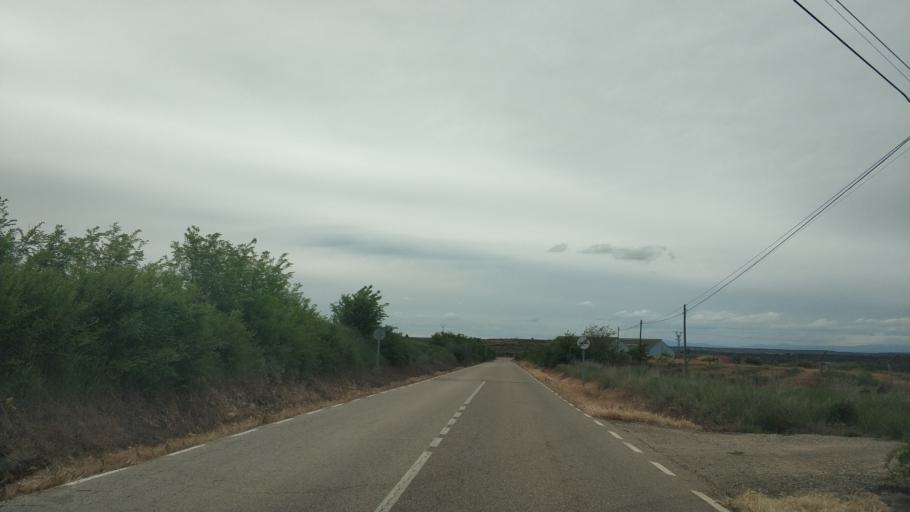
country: ES
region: Castille and Leon
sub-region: Provincia de Soria
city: Berlanga de Duero
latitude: 41.4752
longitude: -2.8612
